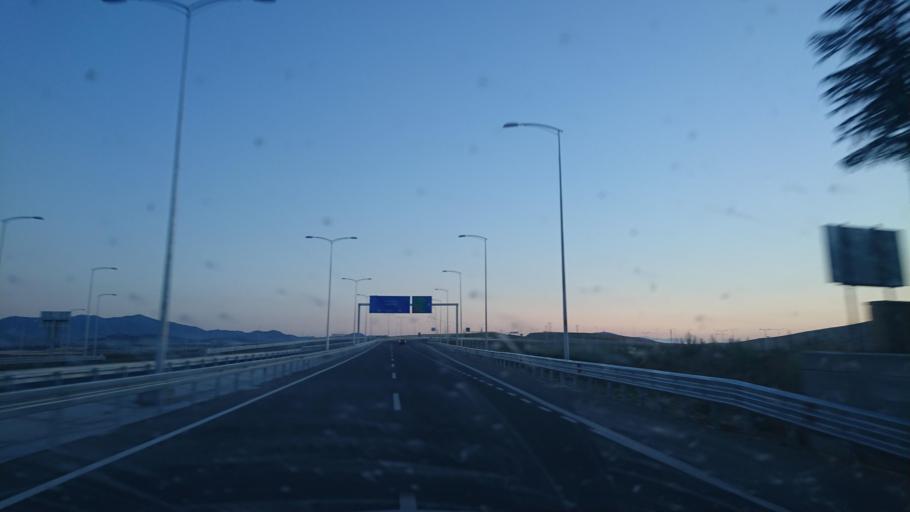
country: TR
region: Aksaray
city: Balci
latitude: 38.7747
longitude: 34.1088
